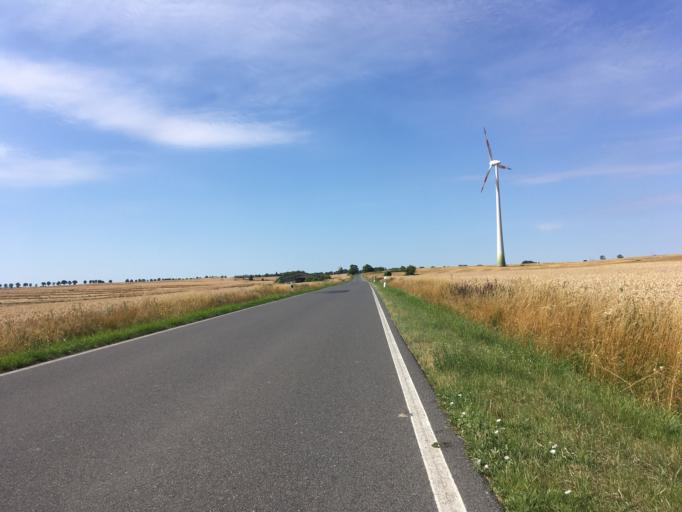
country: DE
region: Brandenburg
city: Gramzow
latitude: 53.2552
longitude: 14.0594
